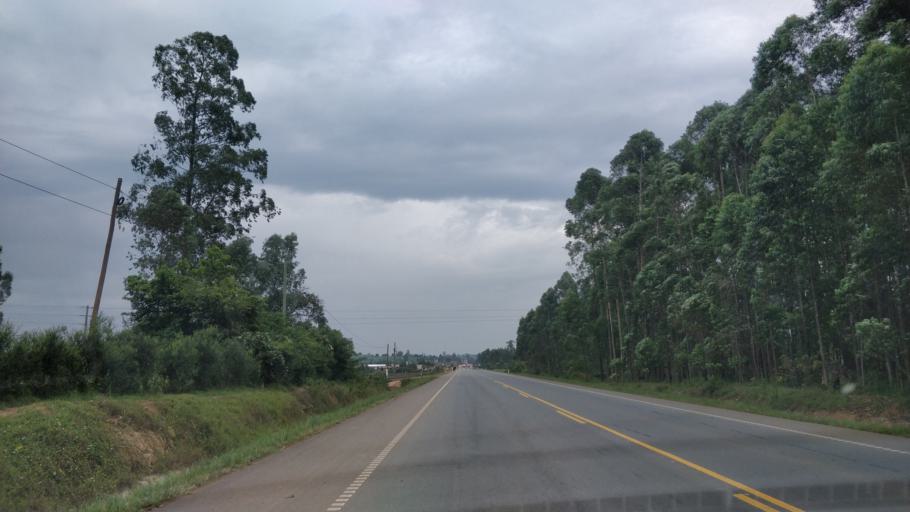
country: UG
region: Western Region
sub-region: Sheema District
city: Kibingo
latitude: -0.6664
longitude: 30.4468
